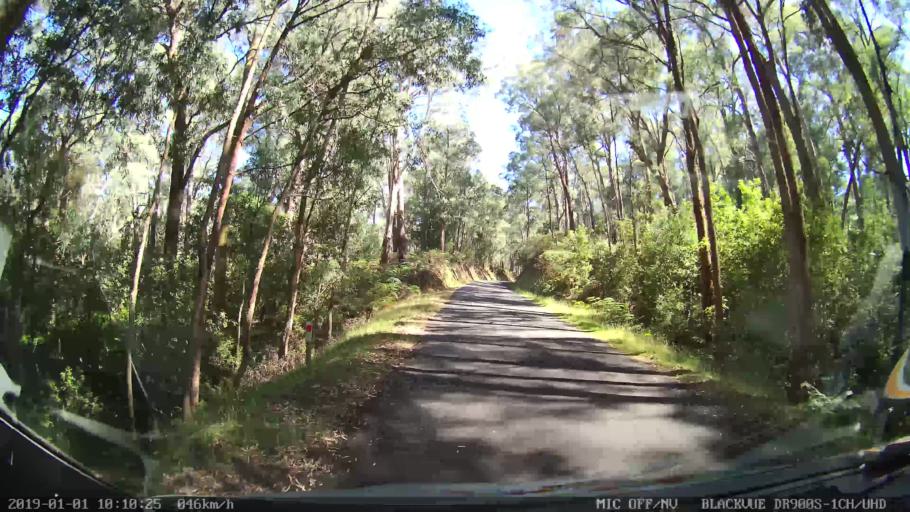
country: AU
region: New South Wales
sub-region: Snowy River
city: Jindabyne
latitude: -36.1413
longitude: 148.1581
